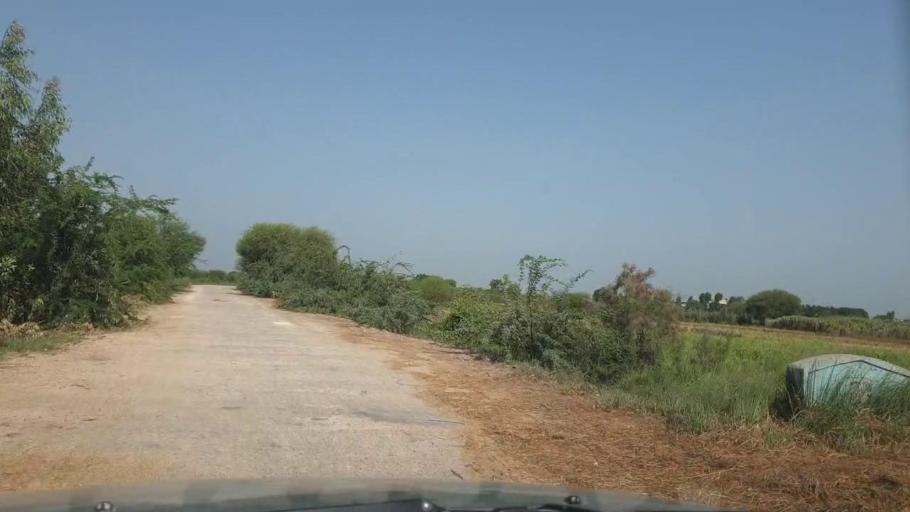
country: PK
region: Sindh
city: Tando Ghulam Ali
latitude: 25.0984
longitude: 68.7660
